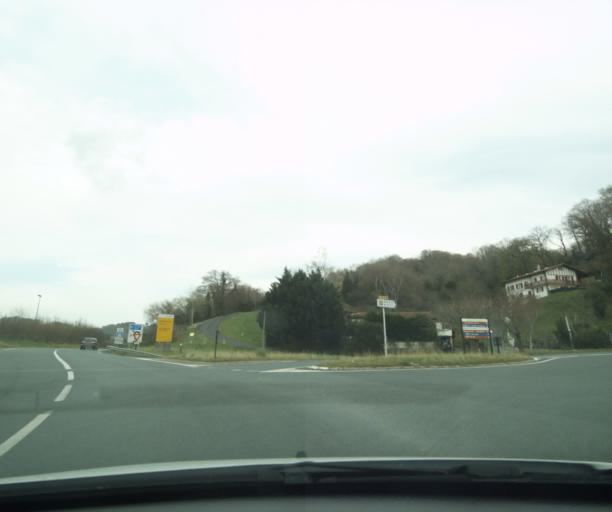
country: ES
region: Basque Country
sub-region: Provincia de Guipuzcoa
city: Irun
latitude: 43.3395
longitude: -1.7516
